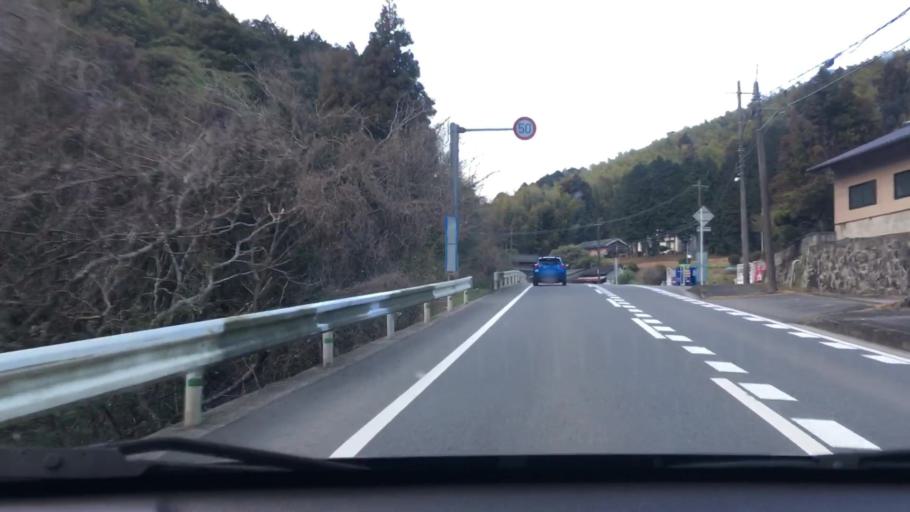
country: JP
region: Oita
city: Hiji
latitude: 33.3717
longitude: 131.4612
